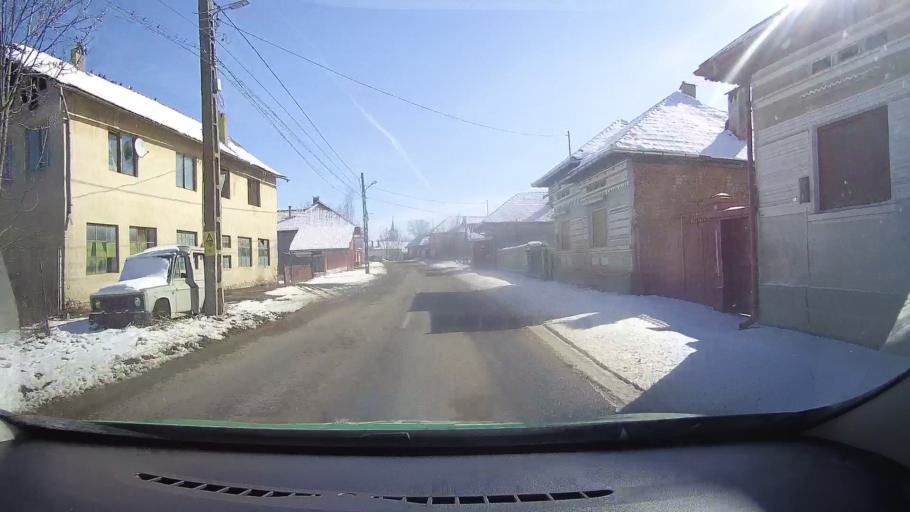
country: RO
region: Brasov
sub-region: Comuna Recea
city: Recea
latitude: 45.7335
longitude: 24.9356
